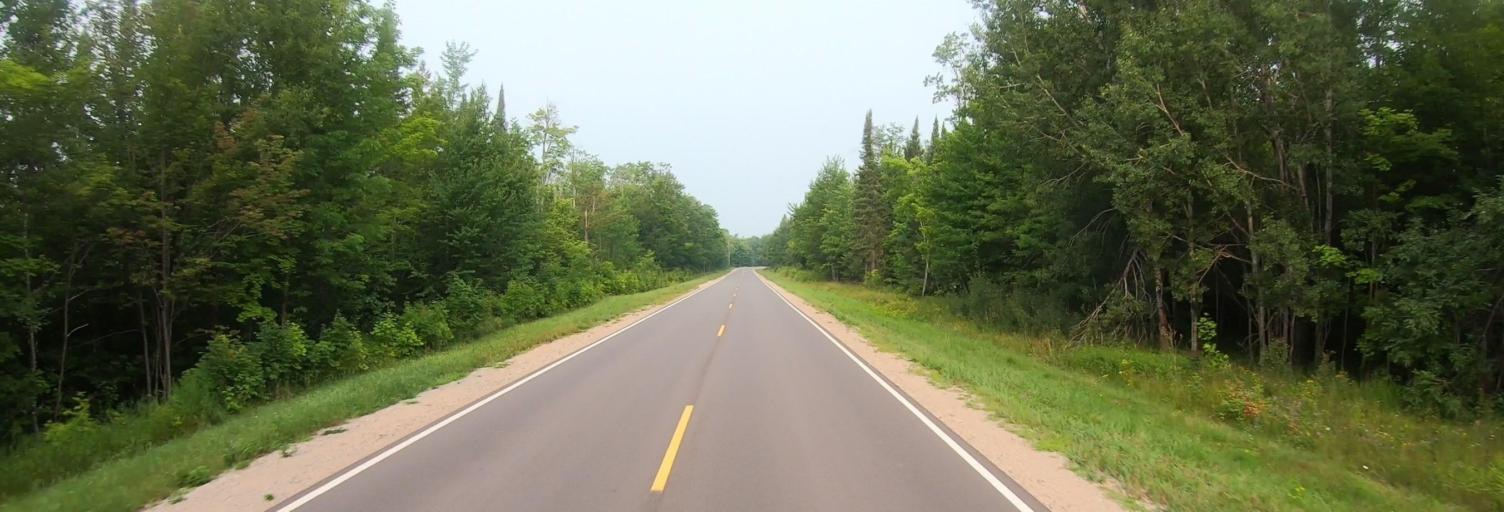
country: US
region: Michigan
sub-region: Luce County
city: Newberry
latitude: 46.4804
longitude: -85.0703
